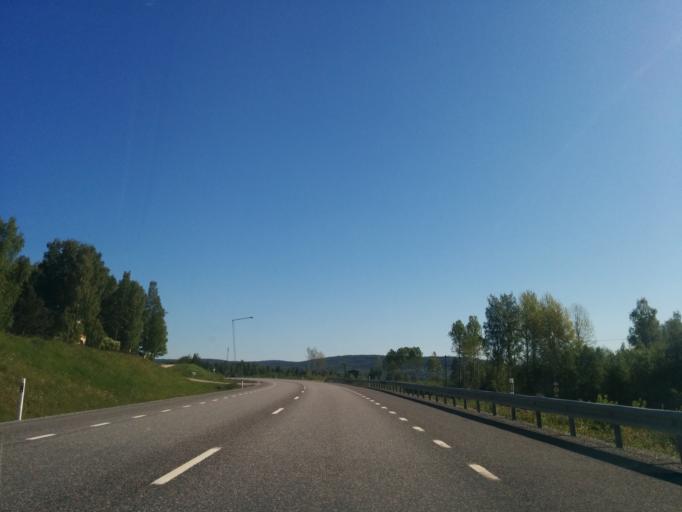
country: SE
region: Vaesternorrland
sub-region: Kramfors Kommun
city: Kramfors
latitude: 62.8335
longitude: 17.8727
